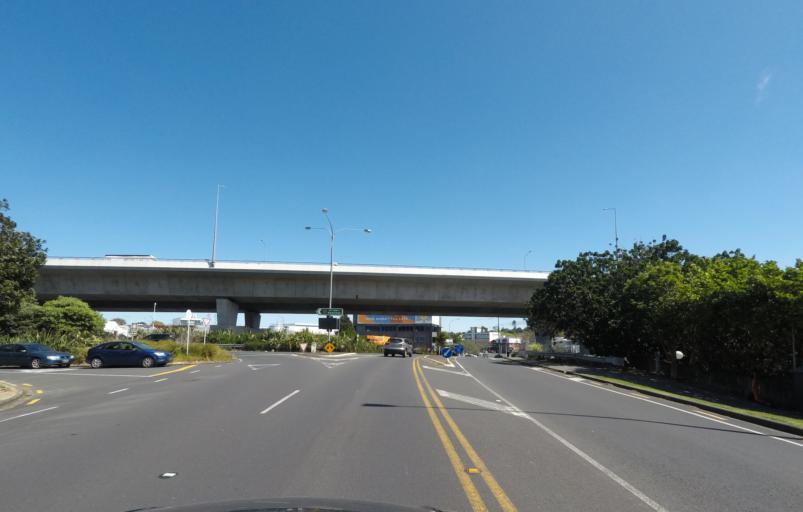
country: NZ
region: Auckland
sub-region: Auckland
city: Auckland
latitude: -36.8743
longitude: 174.7801
